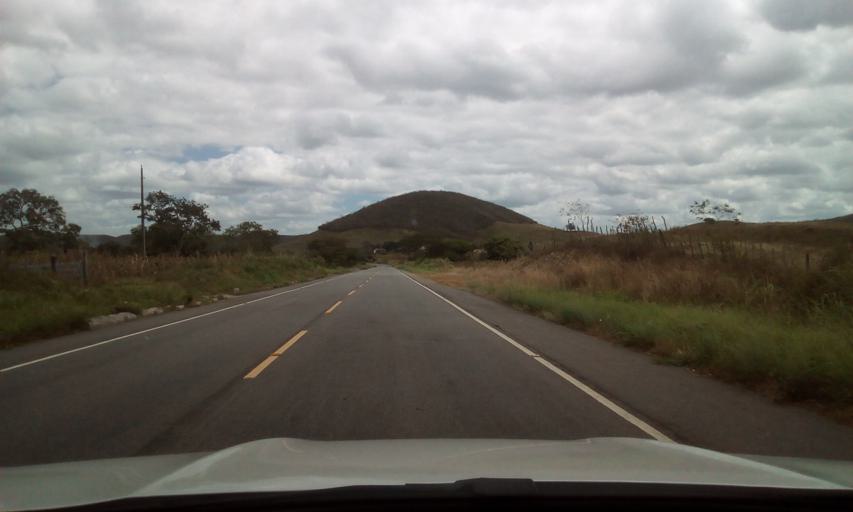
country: BR
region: Paraiba
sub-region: Serra Redonda
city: Alagoa Grande
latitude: -7.1213
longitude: -35.6147
